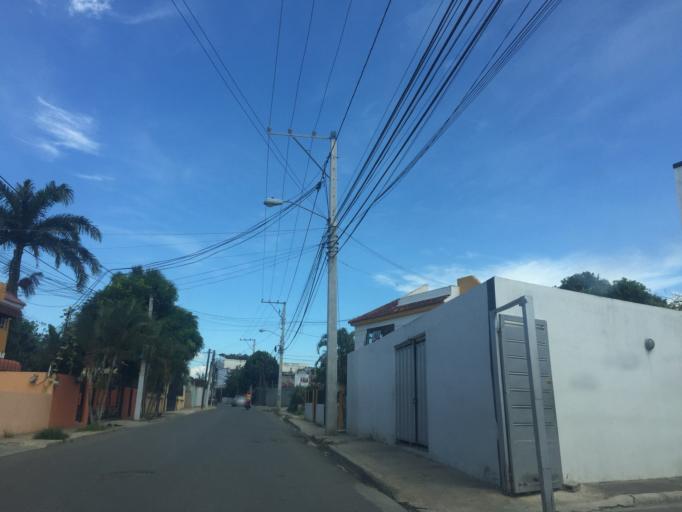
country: DO
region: Santiago
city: Santiago de los Caballeros
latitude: 19.4347
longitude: -70.6753
